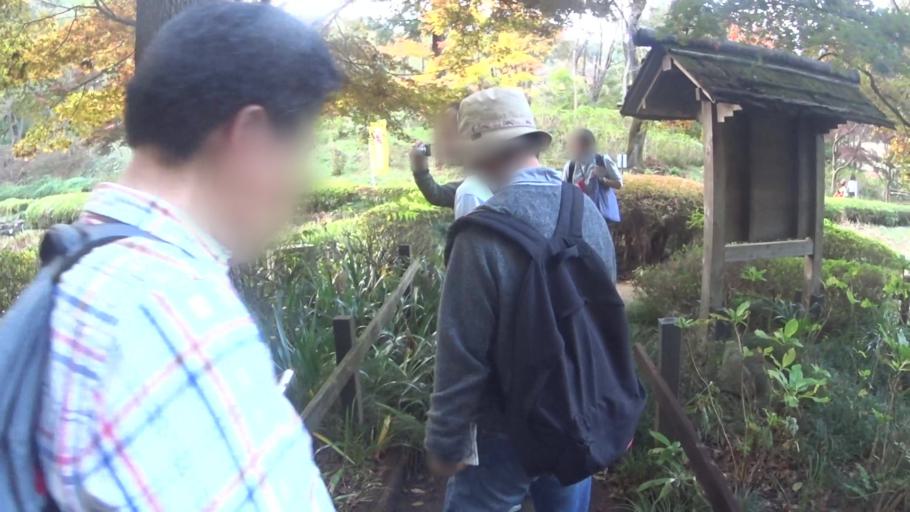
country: JP
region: Tokyo
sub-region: Machida-shi
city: Machida
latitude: 35.5779
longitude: 139.4484
